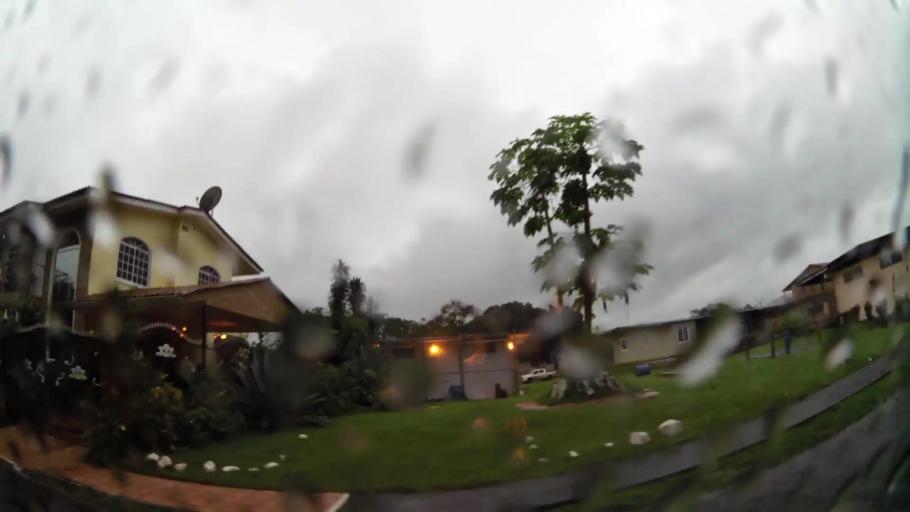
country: PA
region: Panama
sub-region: Distrito de Panama
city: Paraiso
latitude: 9.0271
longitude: -79.6224
